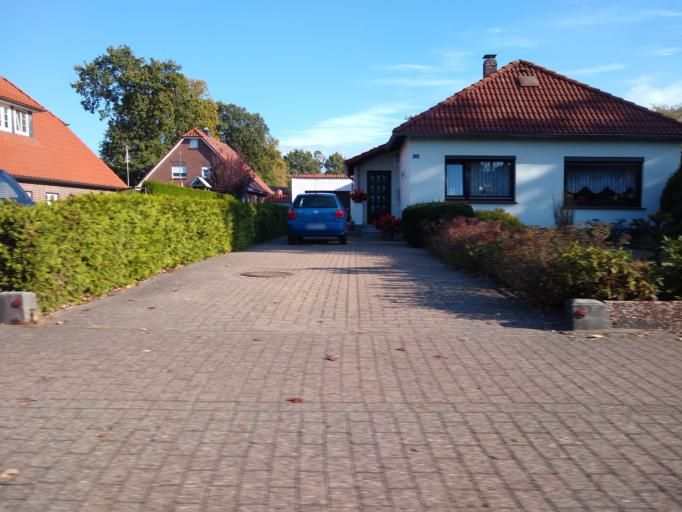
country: DE
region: Lower Saxony
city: Oldenburg
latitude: 53.1893
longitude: 8.2060
